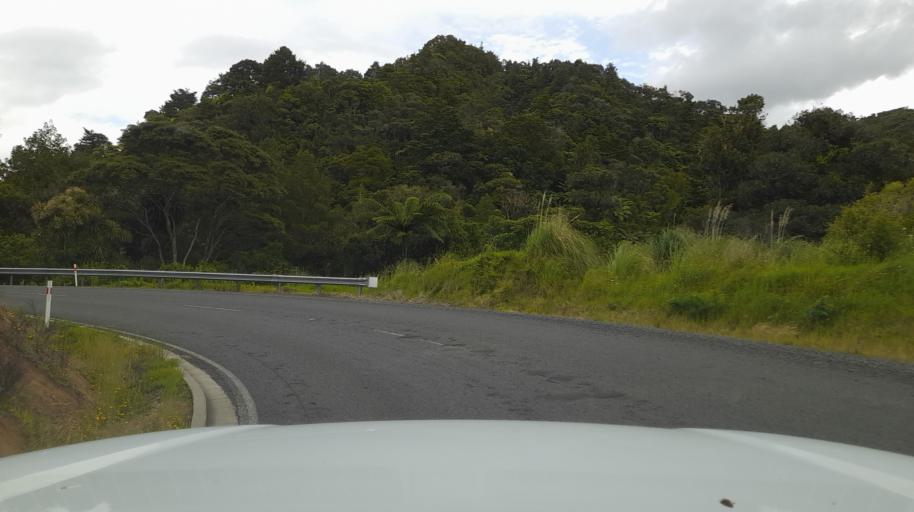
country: NZ
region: Northland
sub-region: Far North District
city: Kaitaia
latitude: -35.3044
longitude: 173.3486
